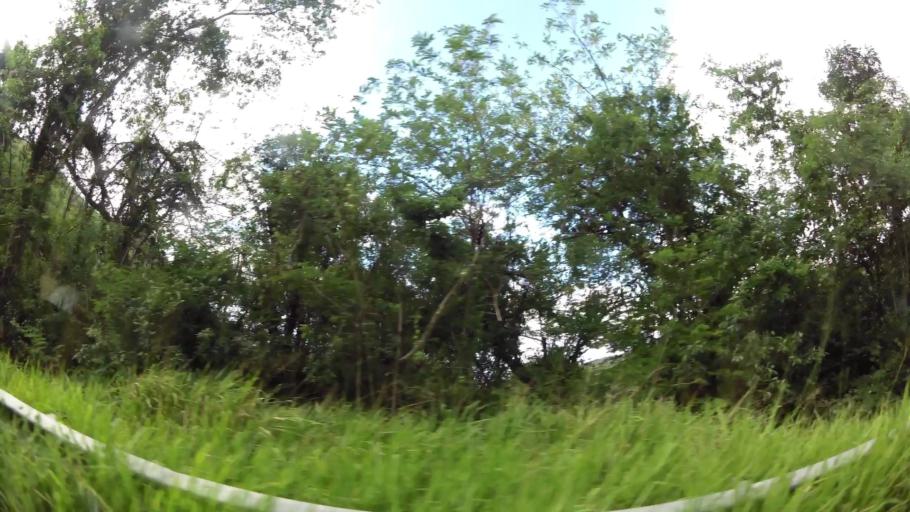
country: MQ
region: Martinique
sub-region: Martinique
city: Les Trois-Ilets
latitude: 14.5079
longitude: -61.0787
